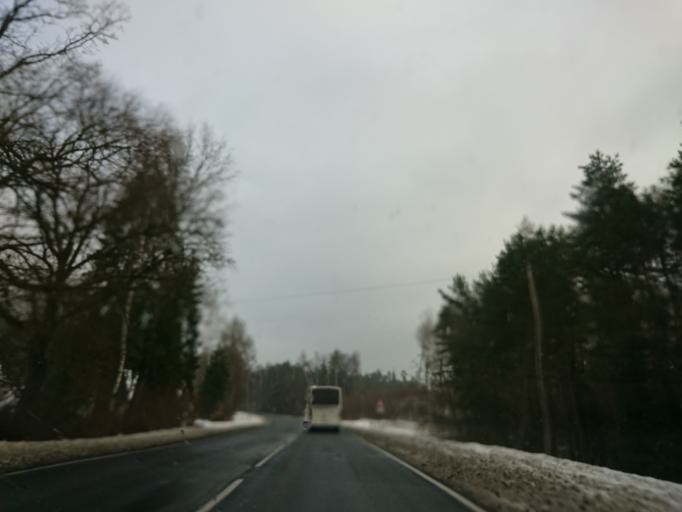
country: LV
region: Pargaujas
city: Stalbe
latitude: 57.2969
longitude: 24.9239
